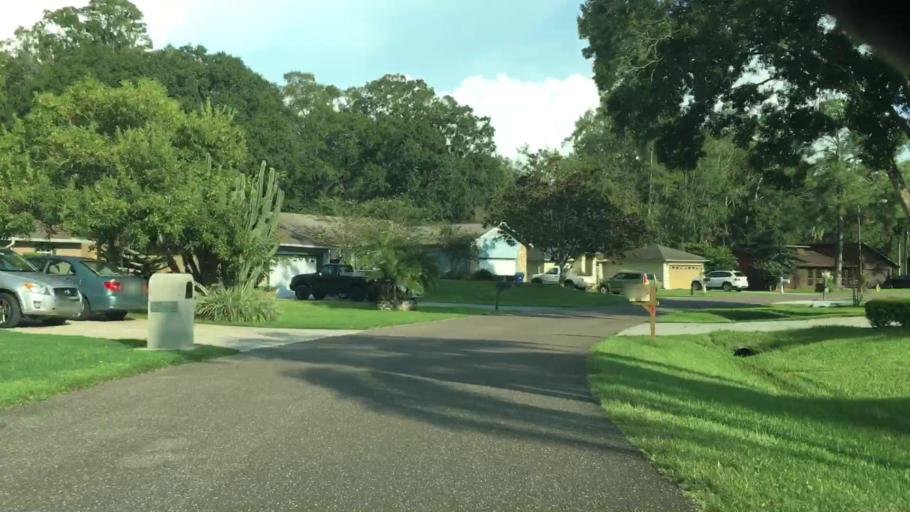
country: US
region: Florida
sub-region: Pasco County
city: Land O' Lakes
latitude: 28.2131
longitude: -82.4201
